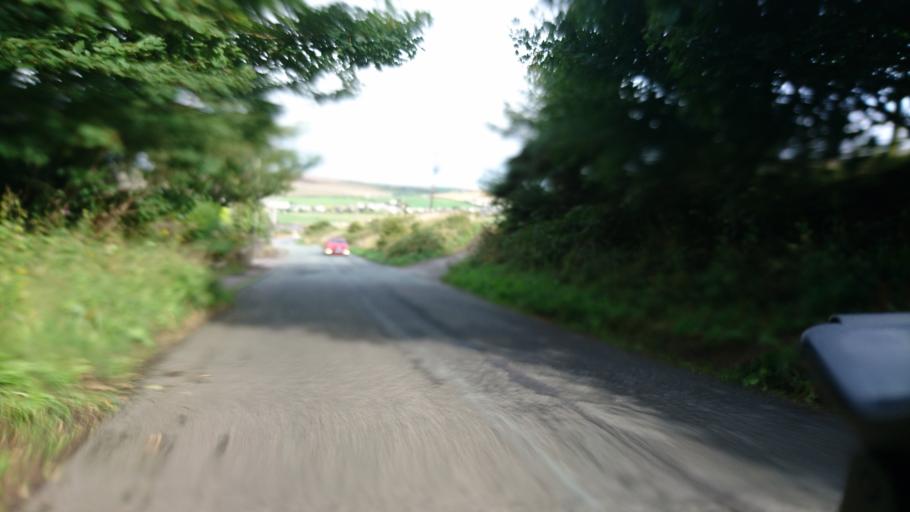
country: GB
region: England
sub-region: Cumbria
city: Saint Bees
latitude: 54.4838
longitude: -3.5860
